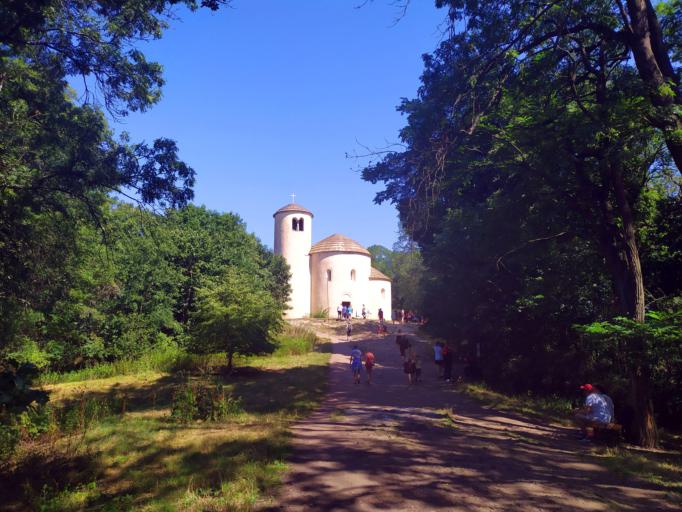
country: CZ
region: Ustecky
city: Roudnice nad Labem
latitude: 50.3859
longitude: 14.2900
